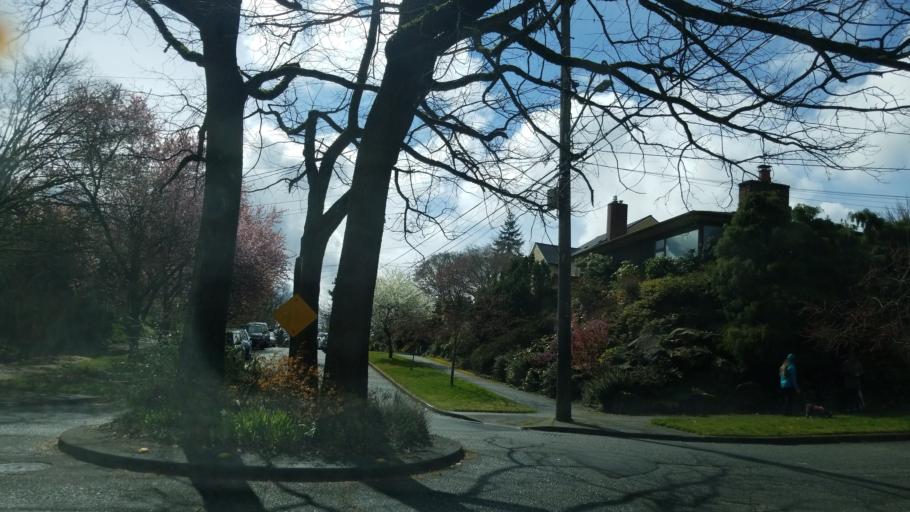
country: US
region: Washington
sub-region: King County
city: Lake Forest Park
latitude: 47.6886
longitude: -122.3090
